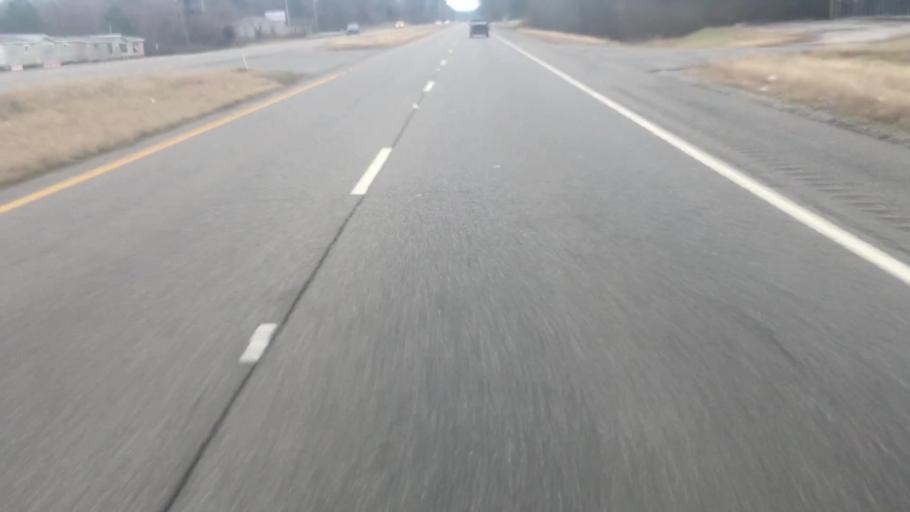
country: US
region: Alabama
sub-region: Walker County
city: Jasper
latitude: 33.8302
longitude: -87.2092
